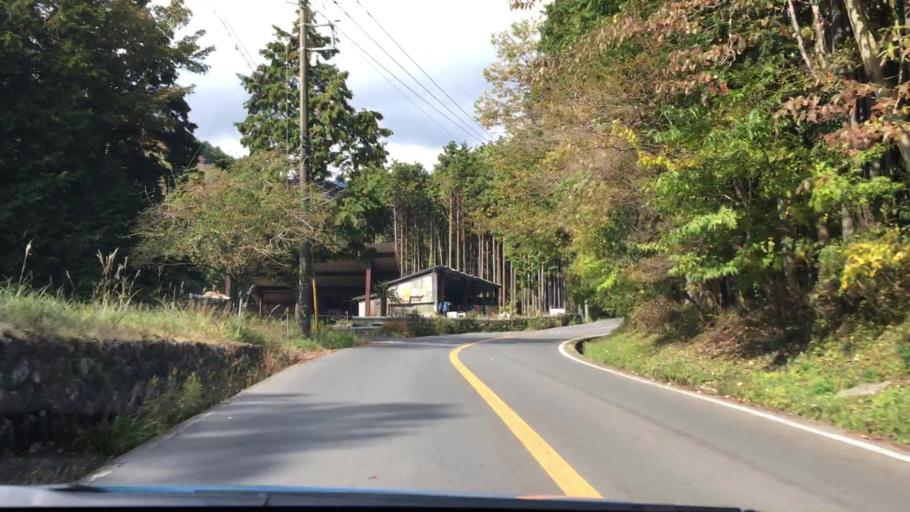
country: JP
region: Shizuoka
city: Gotemba
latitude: 35.3753
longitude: 138.9443
